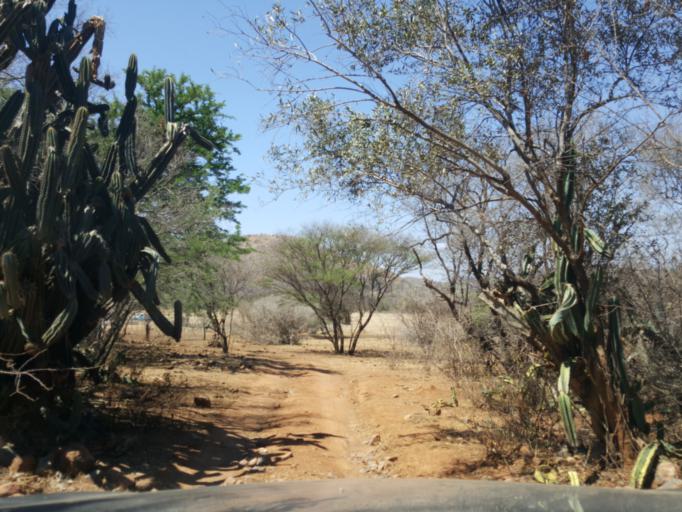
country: BW
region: South East
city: Lobatse
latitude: -25.1577
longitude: 25.6859
